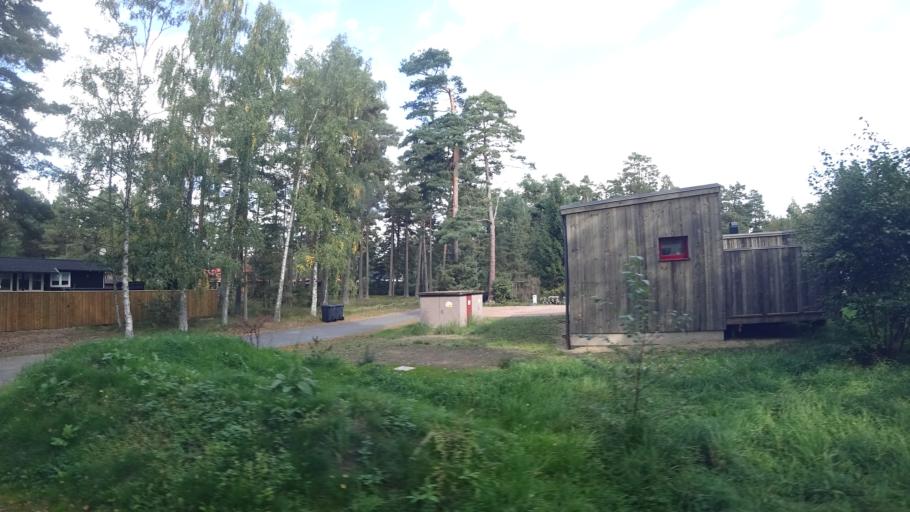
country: SE
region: Skane
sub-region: Kristianstads Kommun
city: Ahus
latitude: 55.9107
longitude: 14.2984
